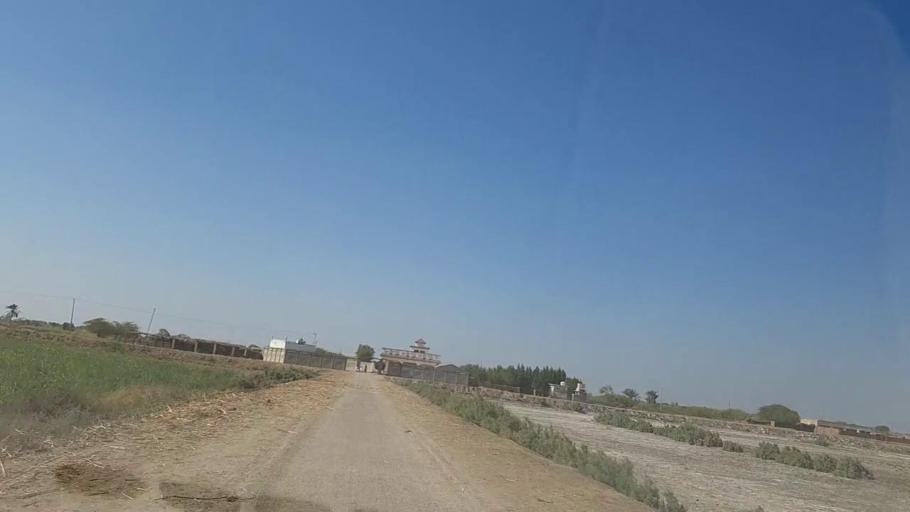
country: PK
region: Sindh
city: Digri
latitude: 25.1269
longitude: 69.0714
